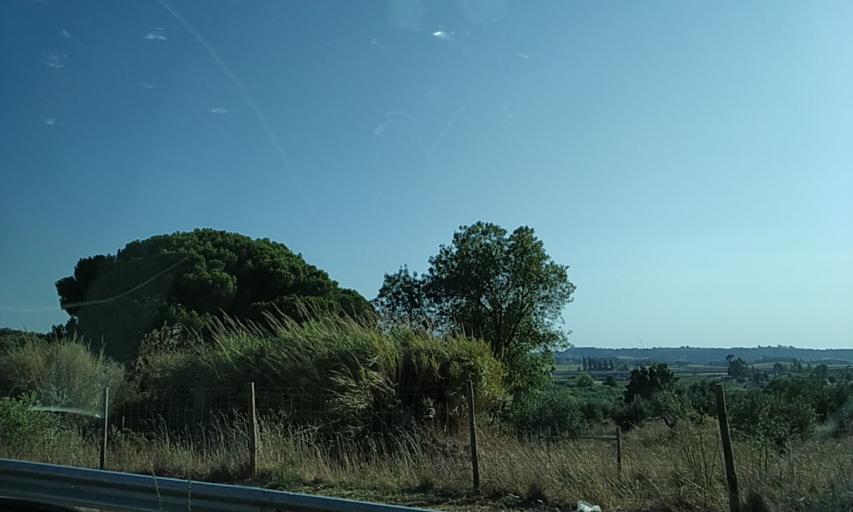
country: PT
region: Santarem
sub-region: Santarem
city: Santarem
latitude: 39.2275
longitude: -8.7038
